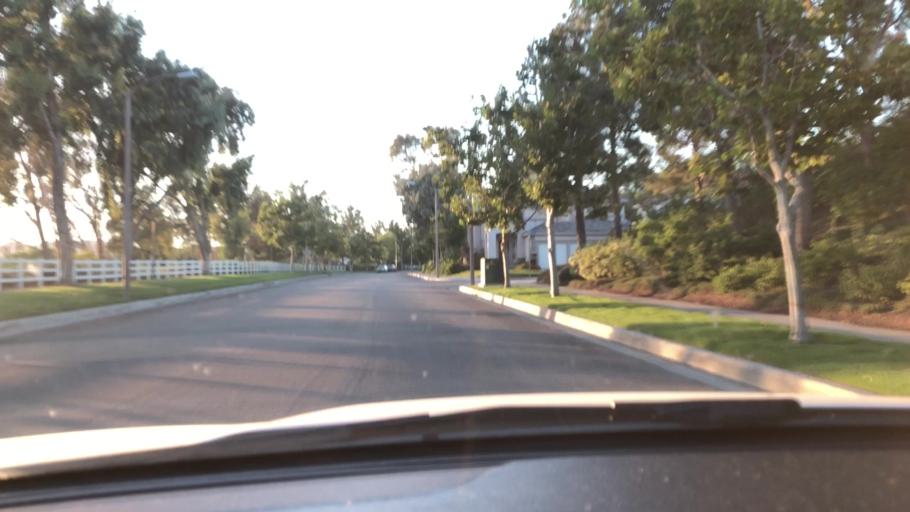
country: US
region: California
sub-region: Los Angeles County
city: Santa Clarita
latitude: 34.4550
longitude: -118.5443
